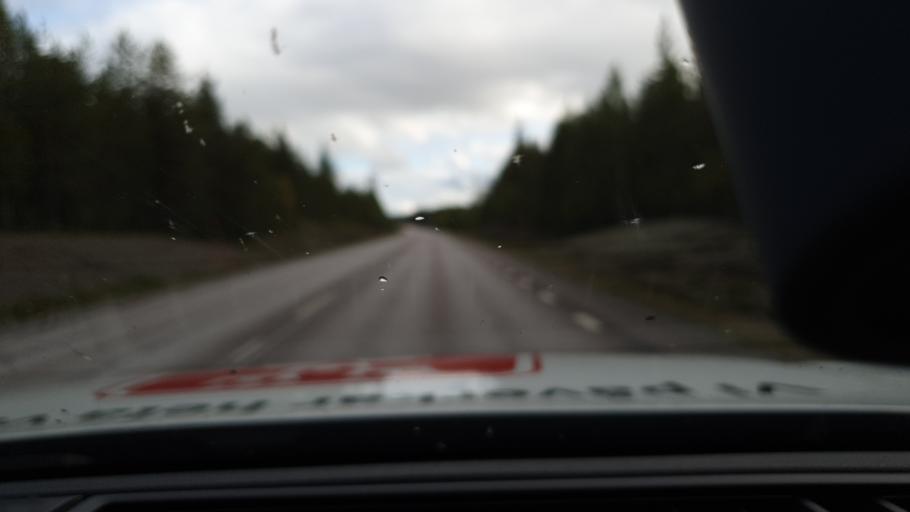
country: SE
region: Norrbotten
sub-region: Gallivare Kommun
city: Gaellivare
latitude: 67.1120
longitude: 20.7924
